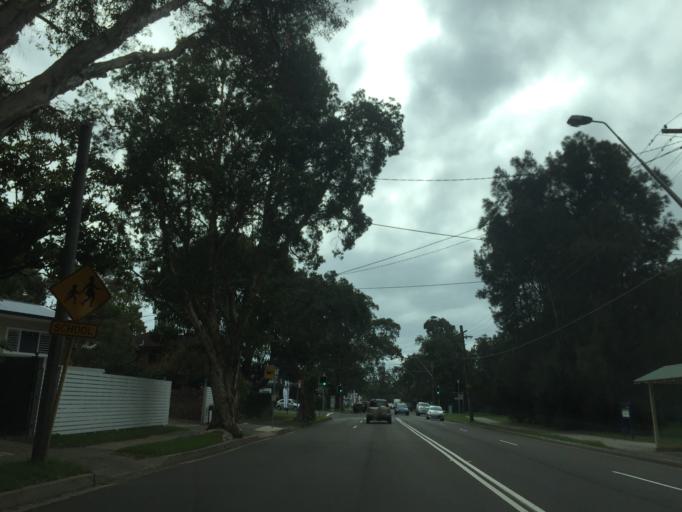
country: AU
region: New South Wales
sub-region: Pittwater
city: North Narrabeen
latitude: -33.7034
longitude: 151.2961
